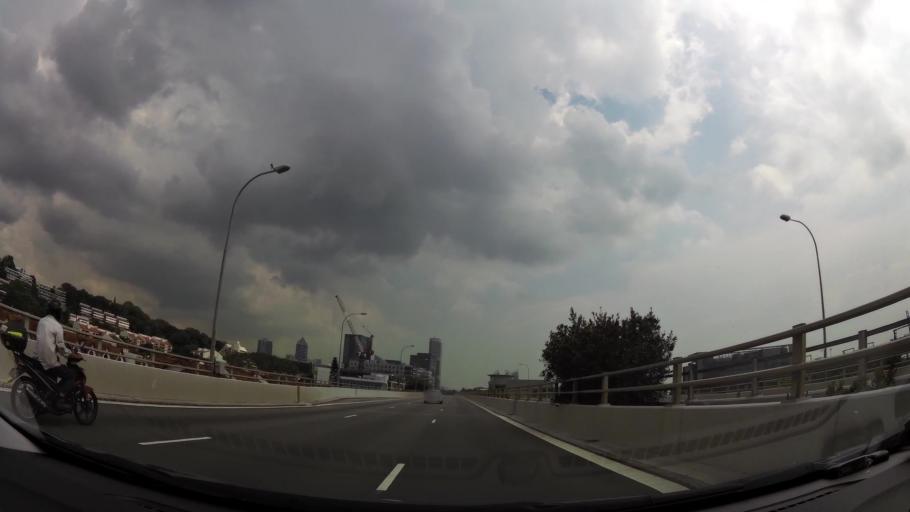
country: SG
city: Singapore
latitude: 1.2772
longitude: 103.7894
